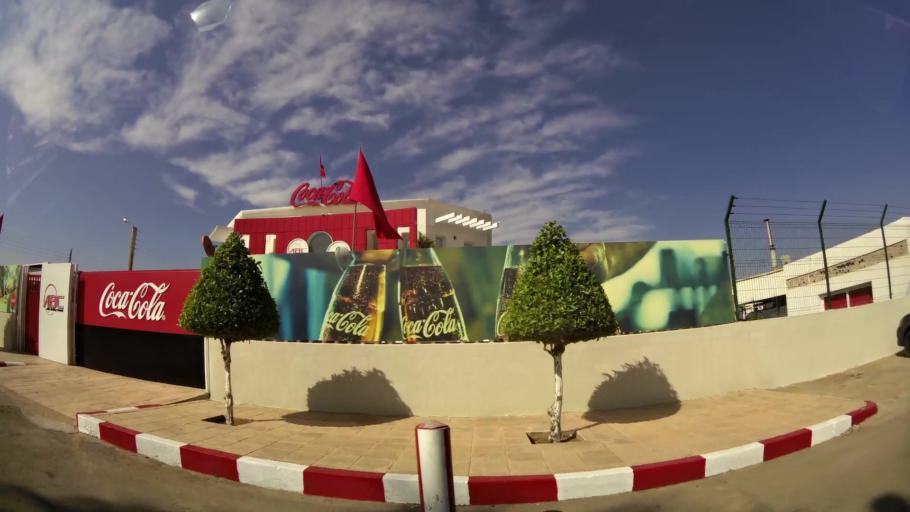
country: MA
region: Oriental
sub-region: Oujda-Angad
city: Oujda
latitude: 34.7051
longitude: -1.8914
